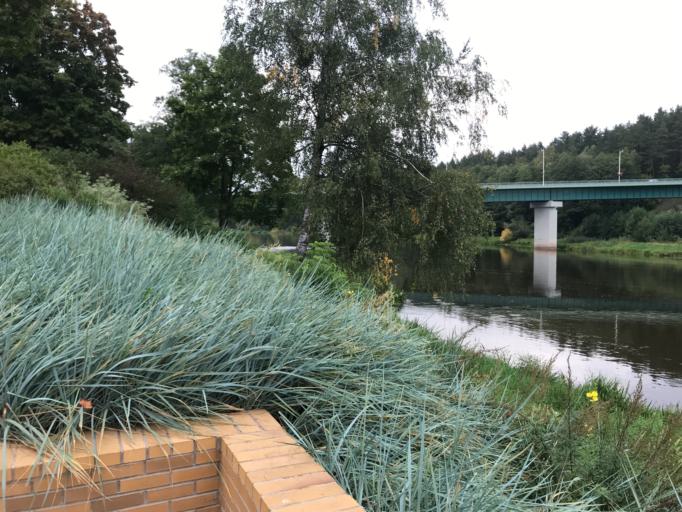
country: LT
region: Alytaus apskritis
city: Druskininkai
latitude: 54.0229
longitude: 23.9769
